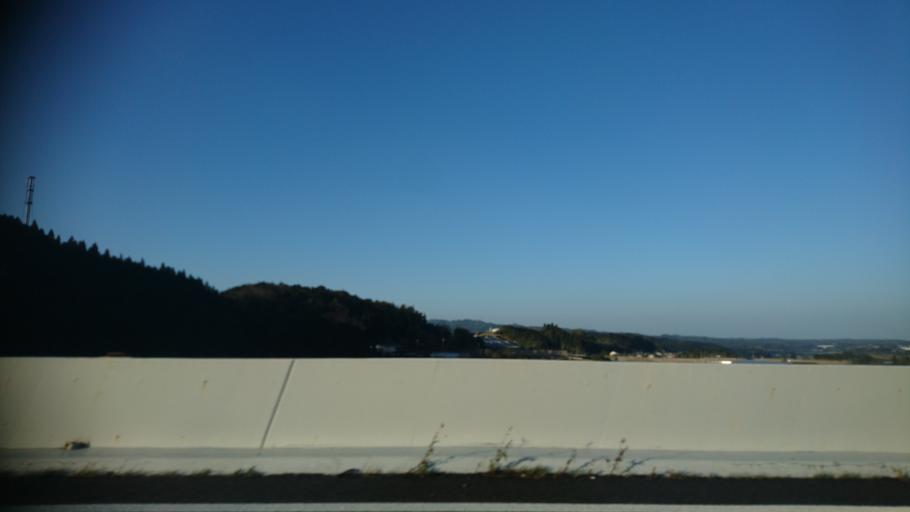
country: JP
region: Miyazaki
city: Miyazaki-shi
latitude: 31.8184
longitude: 131.2652
